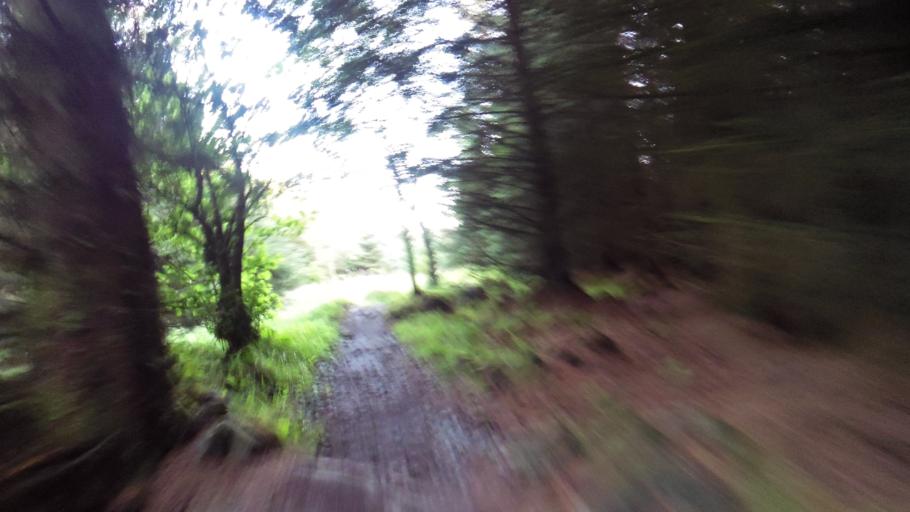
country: GB
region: England
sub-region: North Yorkshire
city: Settle
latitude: 54.0059
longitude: -2.3761
